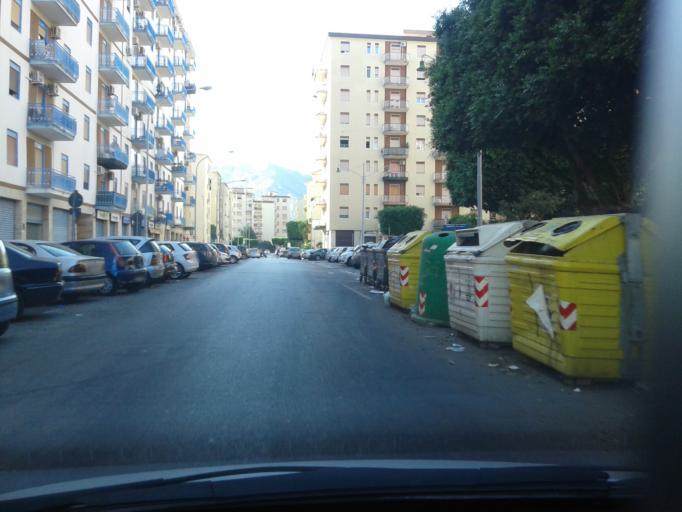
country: IT
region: Sicily
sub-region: Palermo
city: Palermo
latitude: 38.1010
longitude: 13.3348
